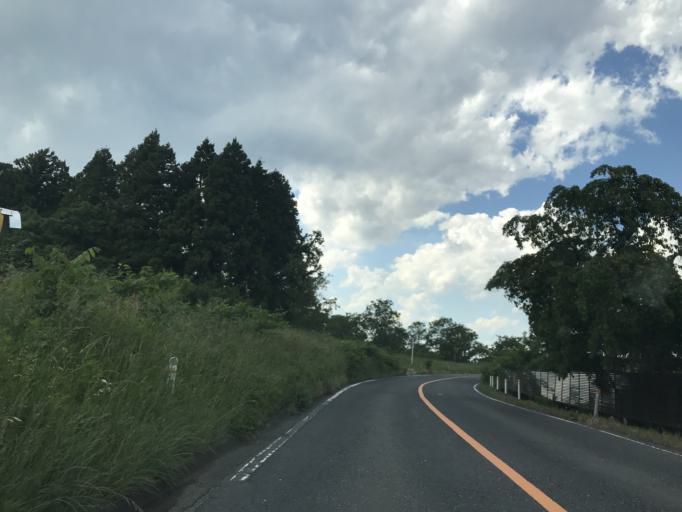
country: JP
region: Miyagi
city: Wakuya
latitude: 38.6560
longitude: 141.2125
